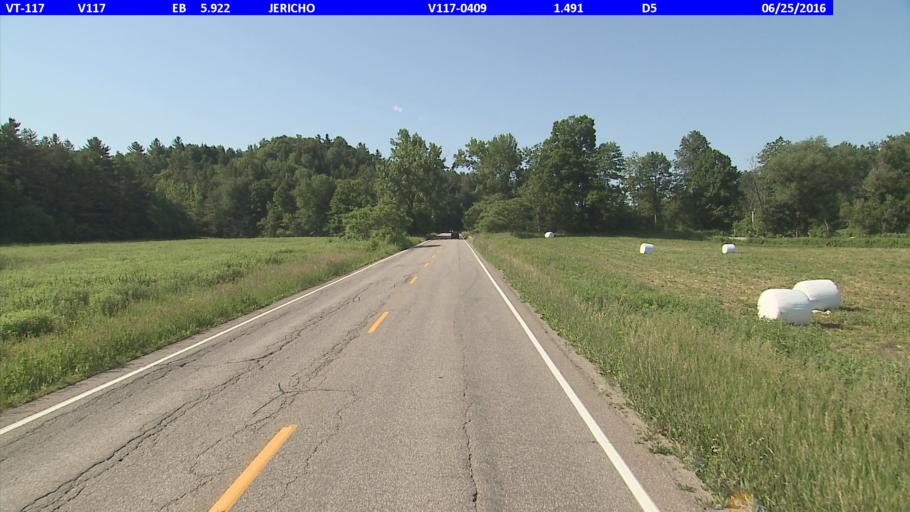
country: US
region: Vermont
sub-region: Chittenden County
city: Williston
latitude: 44.4537
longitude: -73.0179
